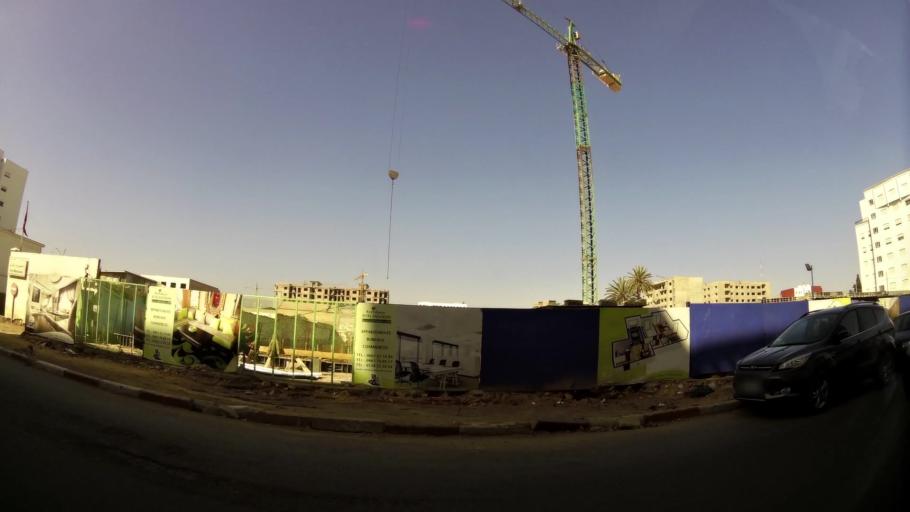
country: MA
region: Souss-Massa-Draa
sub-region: Agadir-Ida-ou-Tnan
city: Agadir
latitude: 30.4183
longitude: -9.5769
